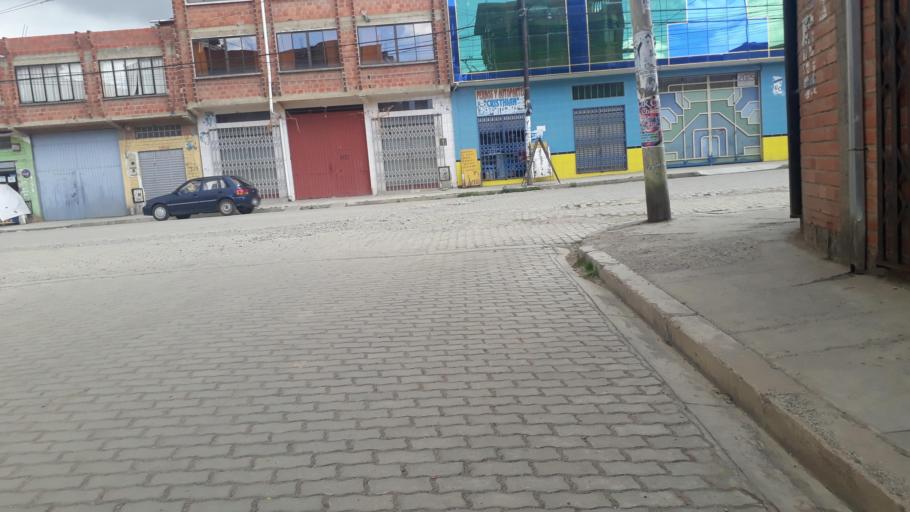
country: BO
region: La Paz
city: La Paz
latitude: -16.4935
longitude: -68.2148
